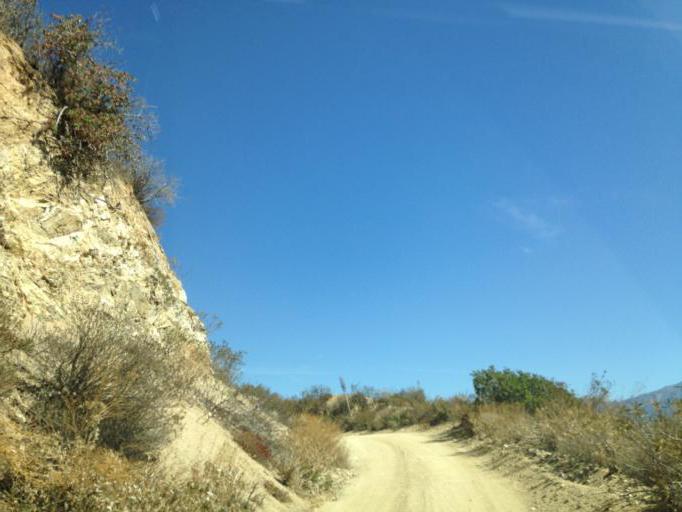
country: US
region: California
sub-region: San Bernardino County
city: Mentone
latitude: 34.1139
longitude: -117.1069
